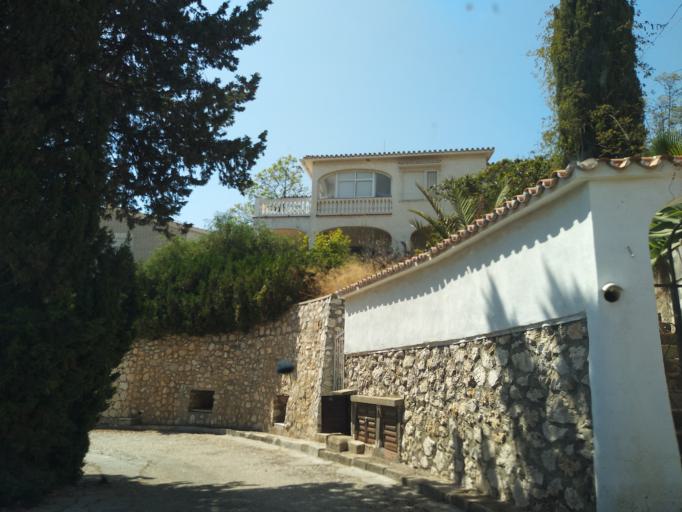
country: ES
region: Andalusia
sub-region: Provincia de Malaga
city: Iznate
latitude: 36.7208
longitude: -4.1885
